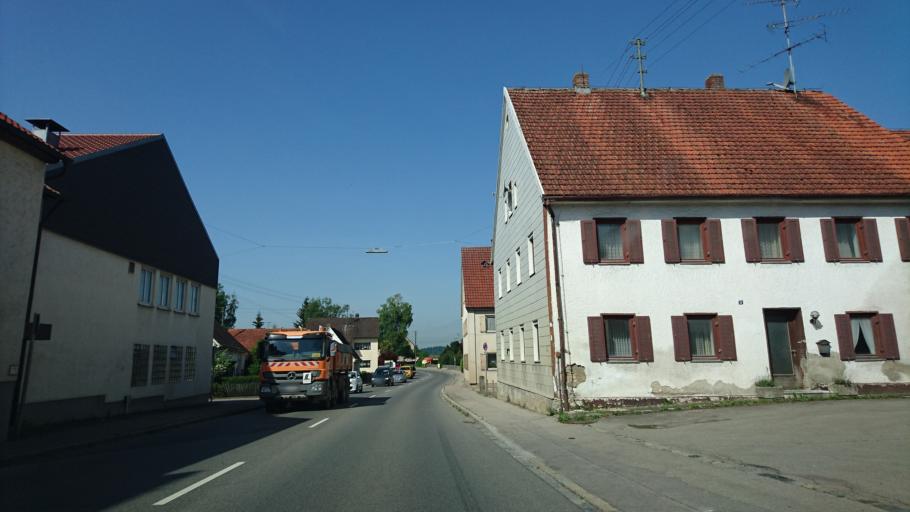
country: DE
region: Bavaria
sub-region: Swabia
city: Diedorf
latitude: 48.3533
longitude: 10.7751
